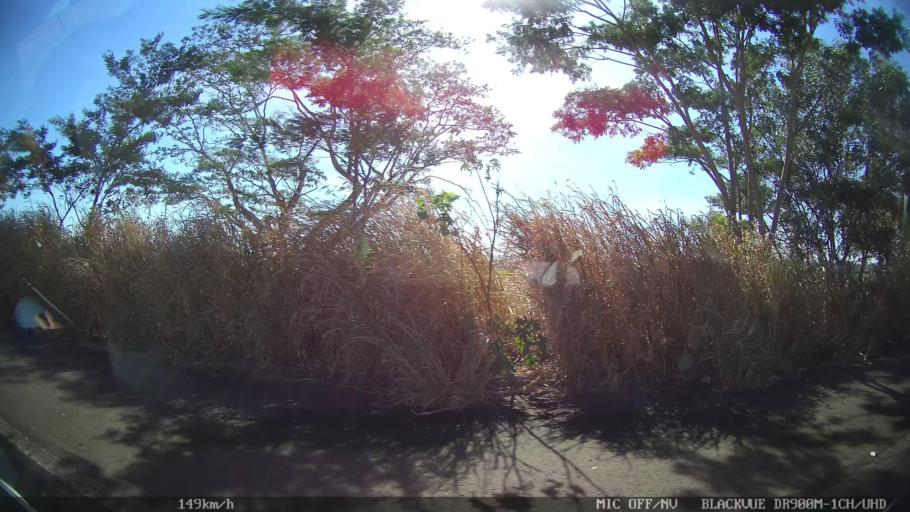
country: BR
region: Sao Paulo
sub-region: Barretos
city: Barretos
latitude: -20.5795
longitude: -48.6872
